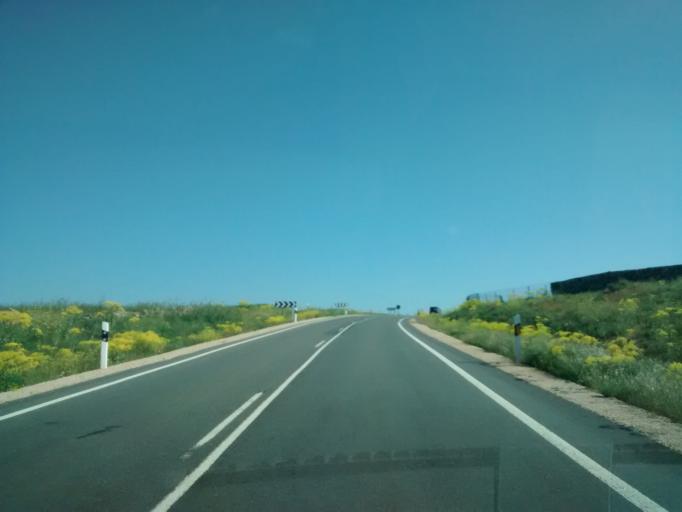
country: ES
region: Castille and Leon
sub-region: Provincia de Segovia
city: Trescasas
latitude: 40.9692
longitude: -4.0322
